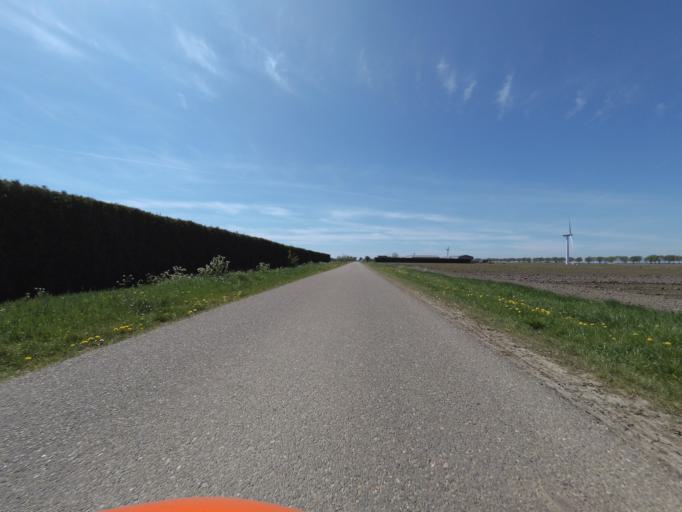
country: NL
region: Flevoland
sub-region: Gemeente Zeewolde
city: Zeewolde
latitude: 52.3554
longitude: 5.4756
